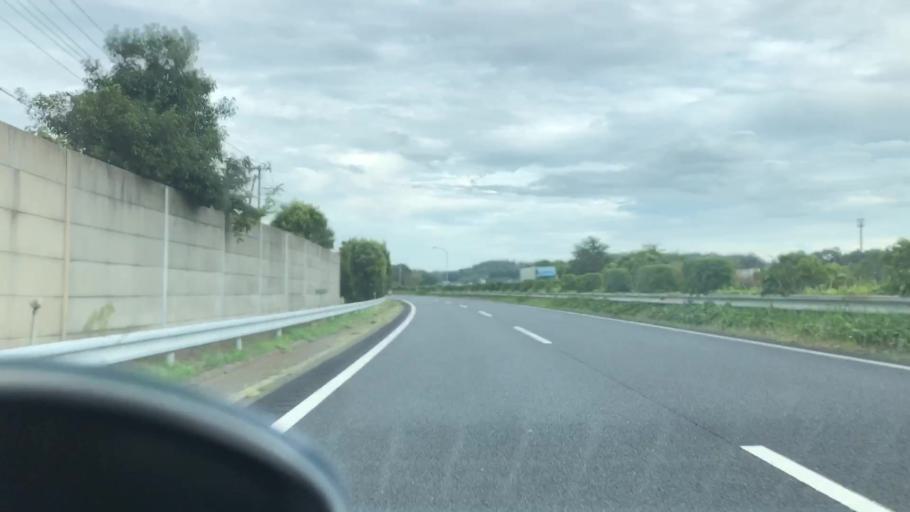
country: JP
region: Hyogo
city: Yashiro
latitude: 34.9209
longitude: 134.9943
